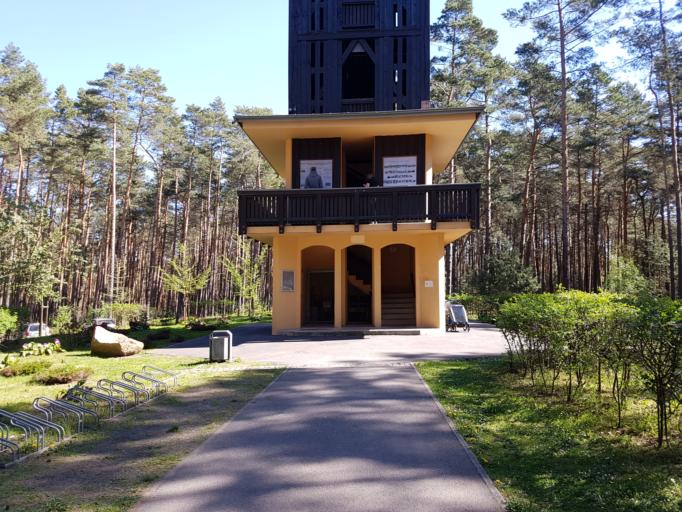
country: DE
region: Brandenburg
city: Groden
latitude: 51.3850
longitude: 13.5776
